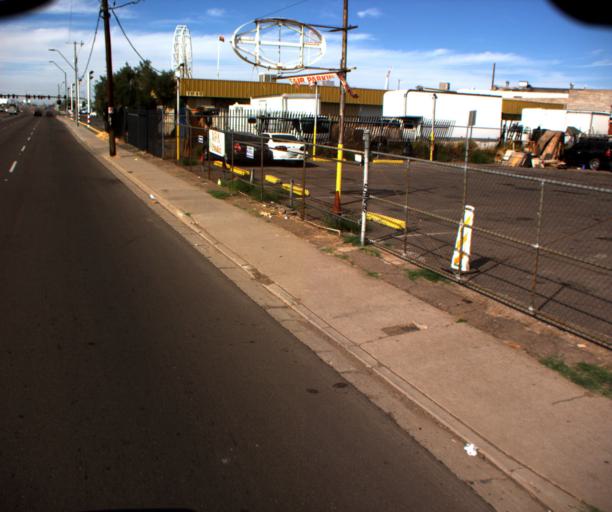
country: US
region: Arizona
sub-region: Maricopa County
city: Phoenix
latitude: 33.4645
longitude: -112.0981
